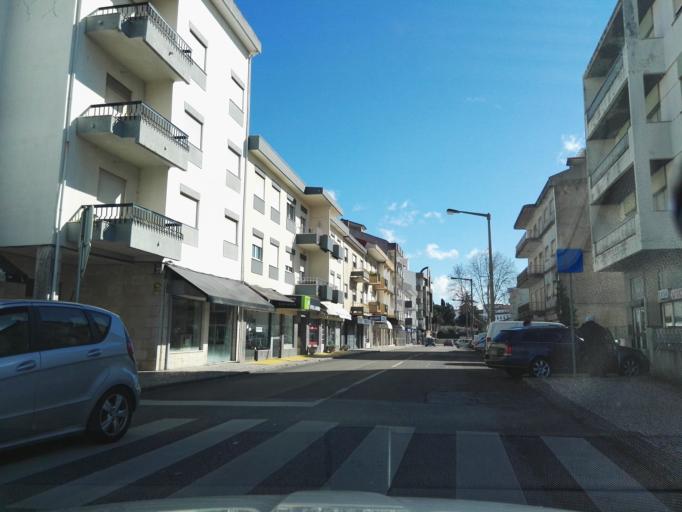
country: PT
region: Santarem
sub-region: Ourem
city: Fatima
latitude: 39.6335
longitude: -8.6809
